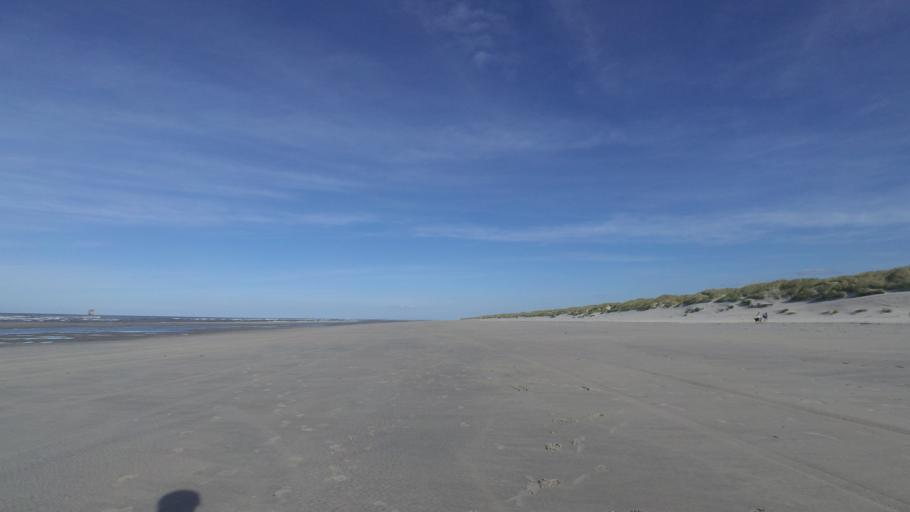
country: NL
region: Friesland
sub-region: Gemeente Ameland
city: Nes
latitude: 53.4641
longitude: 5.8360
